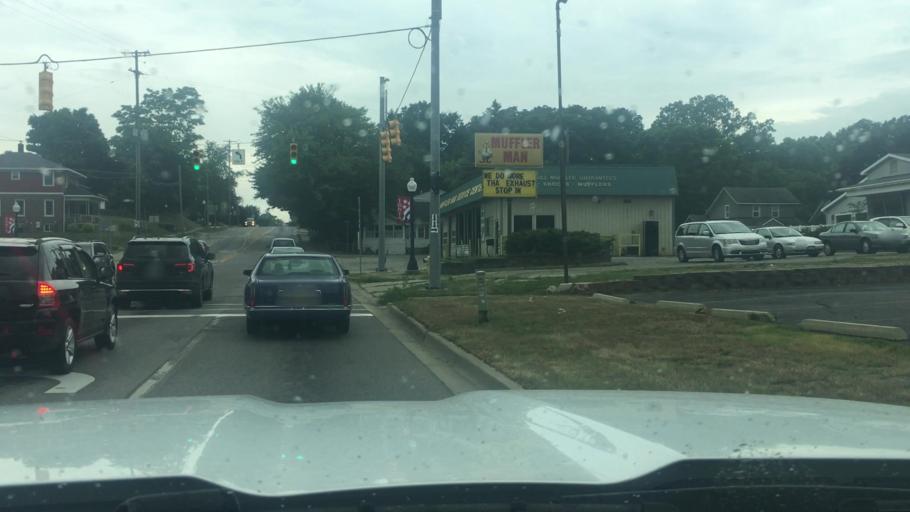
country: US
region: Michigan
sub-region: Ionia County
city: Ionia
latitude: 42.9875
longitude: -85.0705
